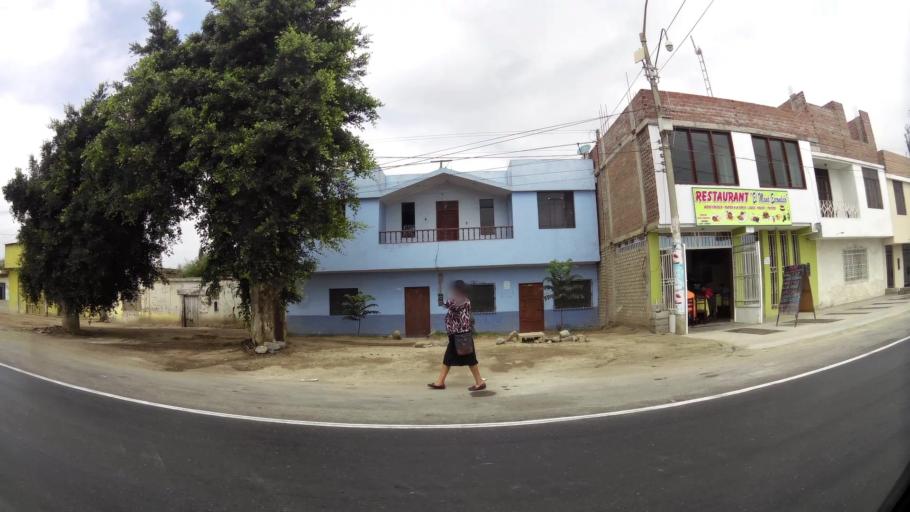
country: PE
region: La Libertad
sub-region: Ascope
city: Chocope
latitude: -7.7916
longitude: -79.2265
